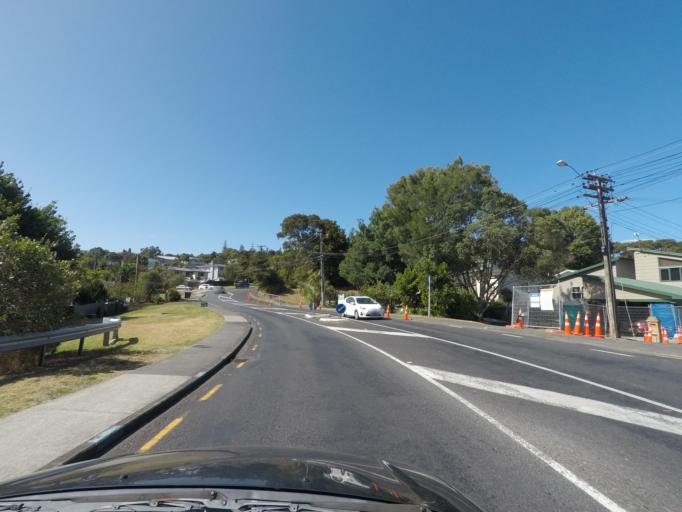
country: NZ
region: Auckland
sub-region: Auckland
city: Waitakere
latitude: -36.9240
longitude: 174.6559
